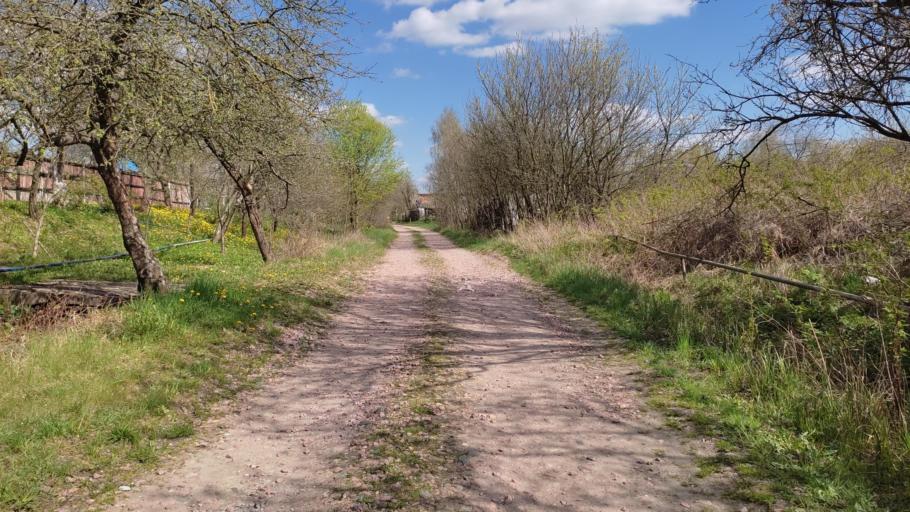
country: BY
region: Grodnenskaya
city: Hrodna
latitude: 53.6567
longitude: 23.8996
